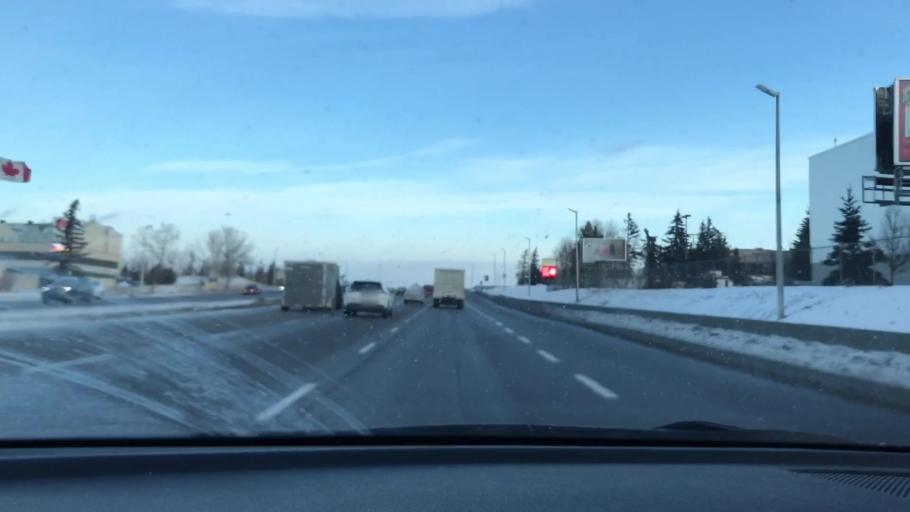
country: CA
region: Alberta
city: Calgary
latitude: 51.0927
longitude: -114.0084
